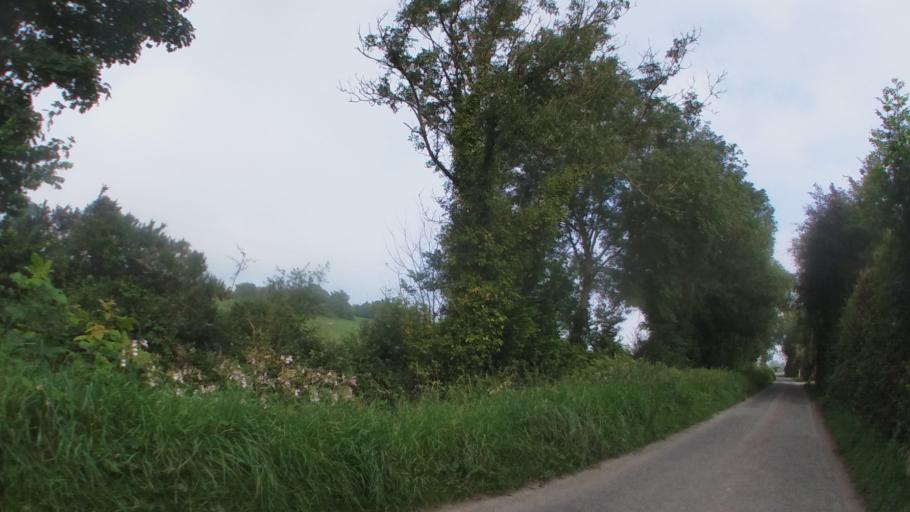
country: IE
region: Leinster
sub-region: Kilkenny
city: Kilkenny
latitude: 52.6909
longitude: -7.1887
